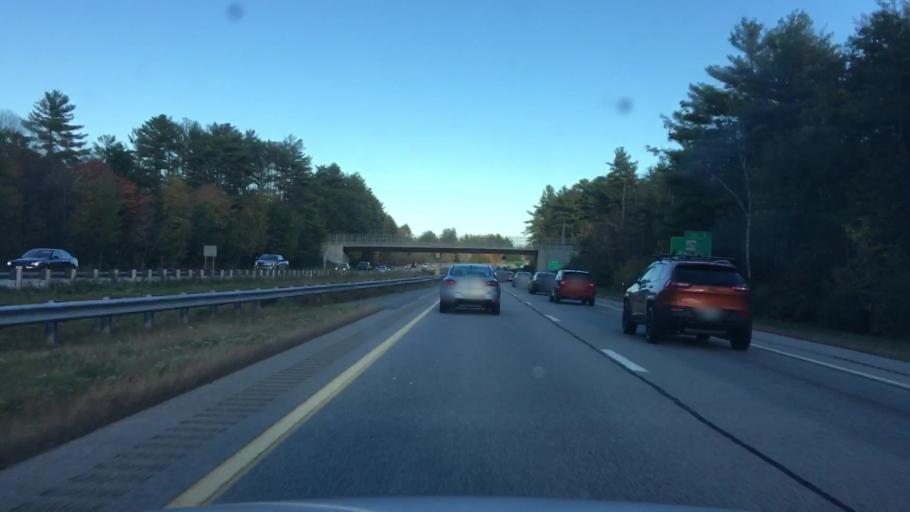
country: US
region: New Hampshire
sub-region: Rockingham County
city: Epping
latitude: 43.0267
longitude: -71.0885
